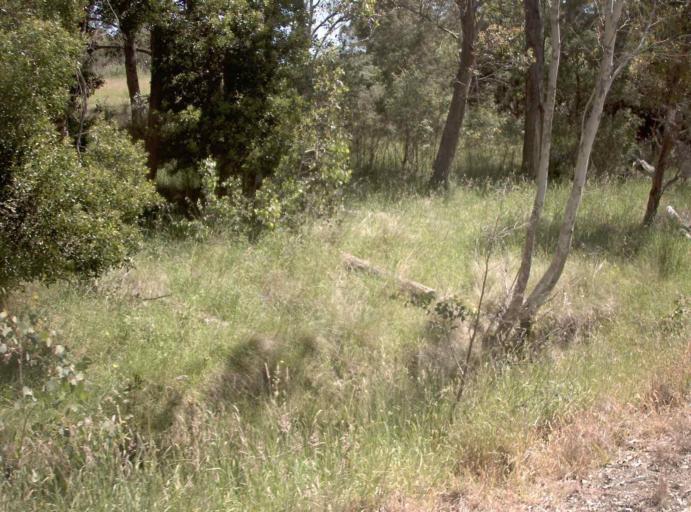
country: AU
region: New South Wales
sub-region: Bombala
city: Bombala
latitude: -37.0608
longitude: 148.8007
